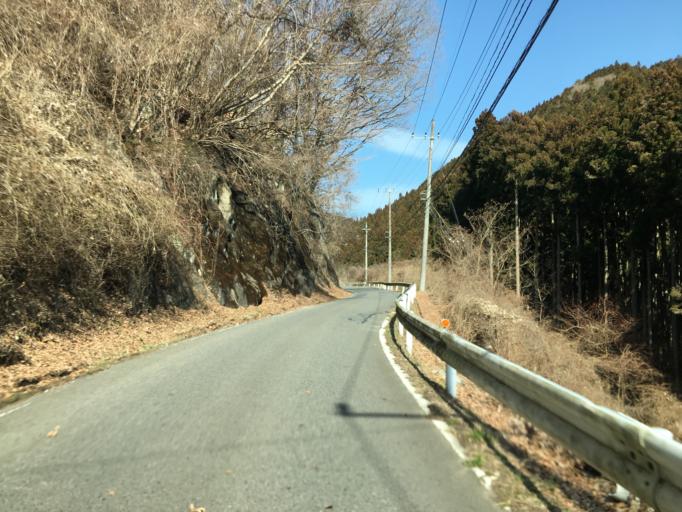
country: JP
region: Ibaraki
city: Daigo
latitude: 36.8046
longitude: 140.4969
